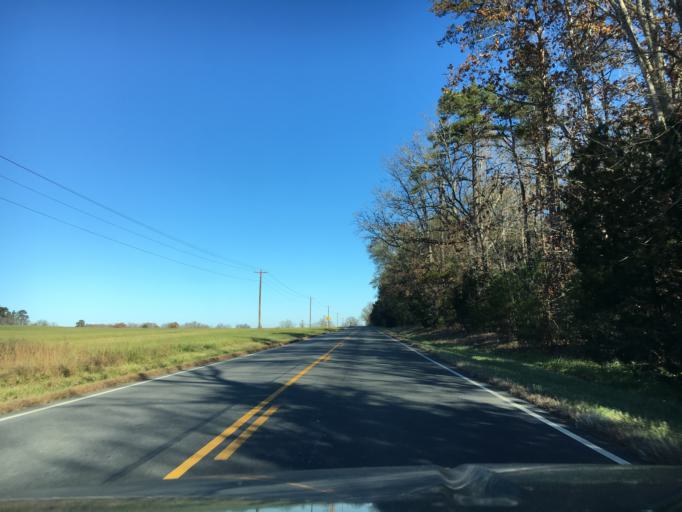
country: US
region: Virginia
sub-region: Buckingham County
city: Buckingham
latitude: 37.5303
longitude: -78.6159
